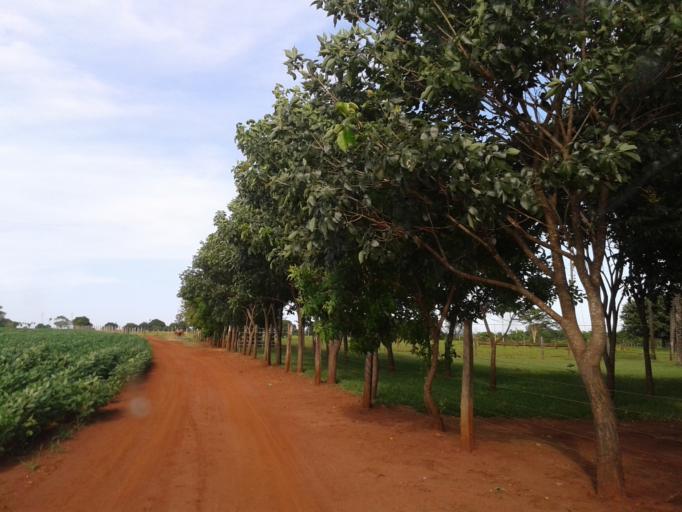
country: BR
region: Minas Gerais
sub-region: Centralina
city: Centralina
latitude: -18.7125
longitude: -49.1914
